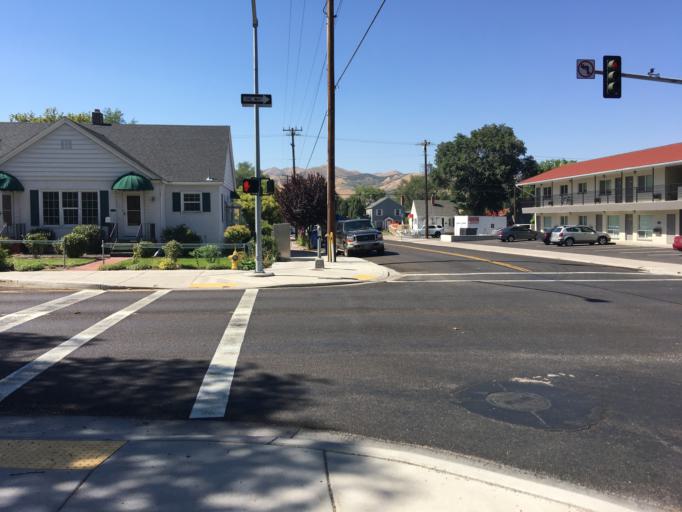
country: US
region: Idaho
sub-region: Bannock County
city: Pocatello
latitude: 42.8621
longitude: -112.4382
